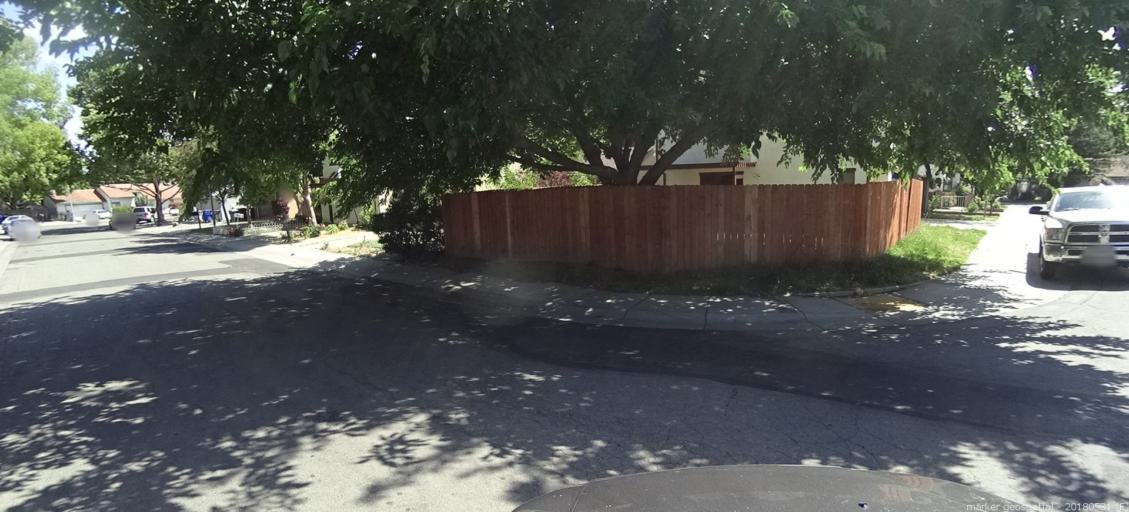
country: US
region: California
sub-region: Sacramento County
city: Sacramento
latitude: 38.6266
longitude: -121.4948
